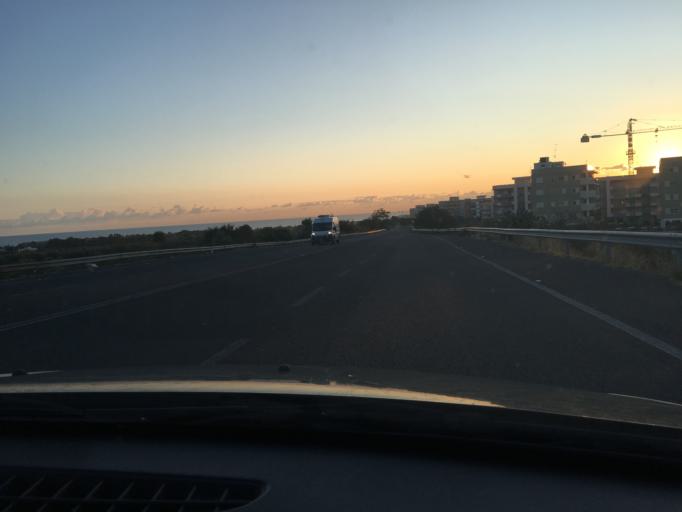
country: IT
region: Apulia
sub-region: Provincia di Bari
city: San Paolo
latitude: 41.1516
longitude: 16.7477
